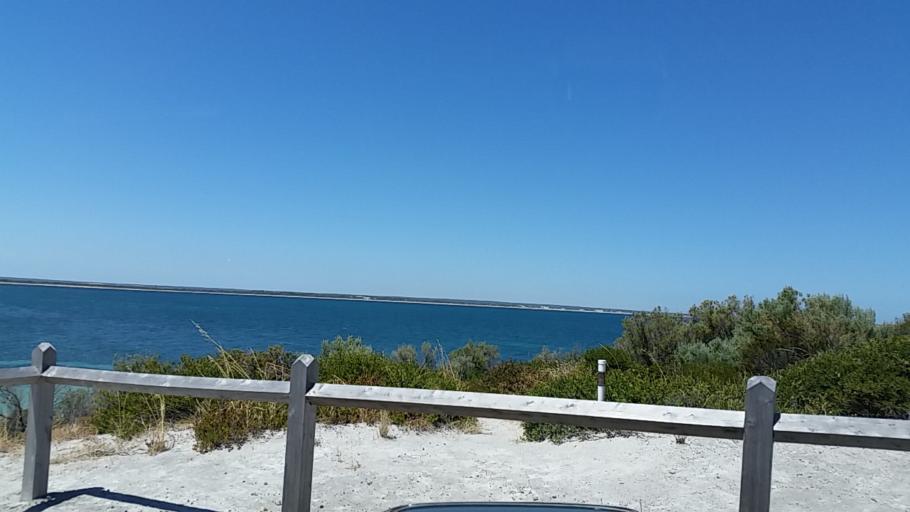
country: AU
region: South Australia
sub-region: Yorke Peninsula
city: Honiton
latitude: -35.2475
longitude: 136.9817
